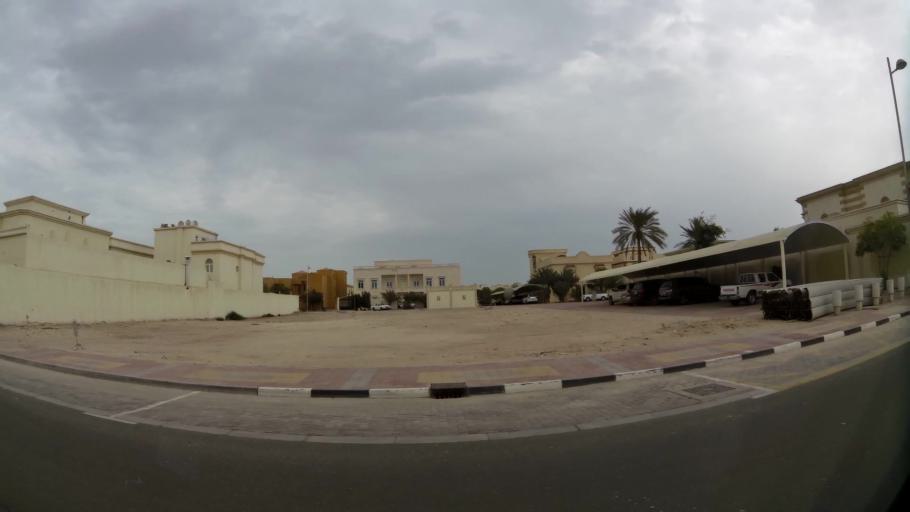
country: QA
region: Baladiyat ad Dawhah
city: Doha
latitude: 25.3399
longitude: 51.4835
